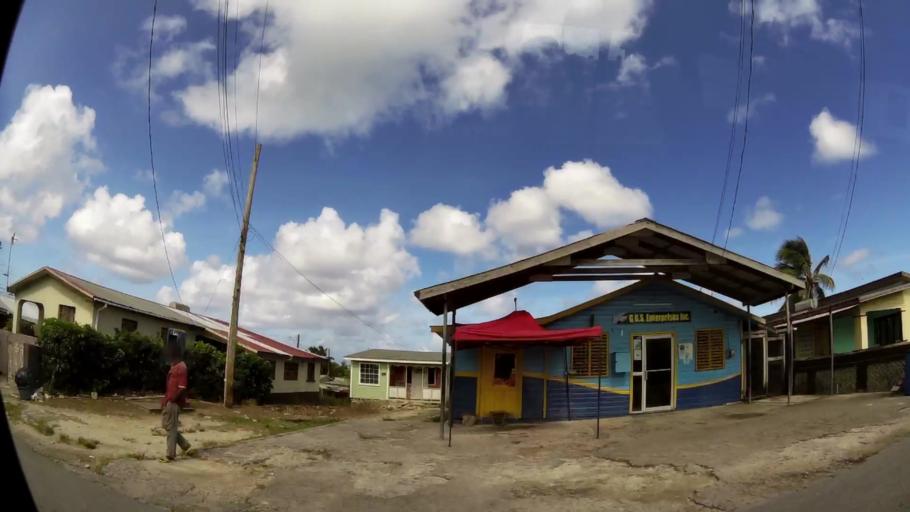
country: BB
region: Saint Lucy
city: Checker Hall
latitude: 13.2811
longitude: -59.6460
